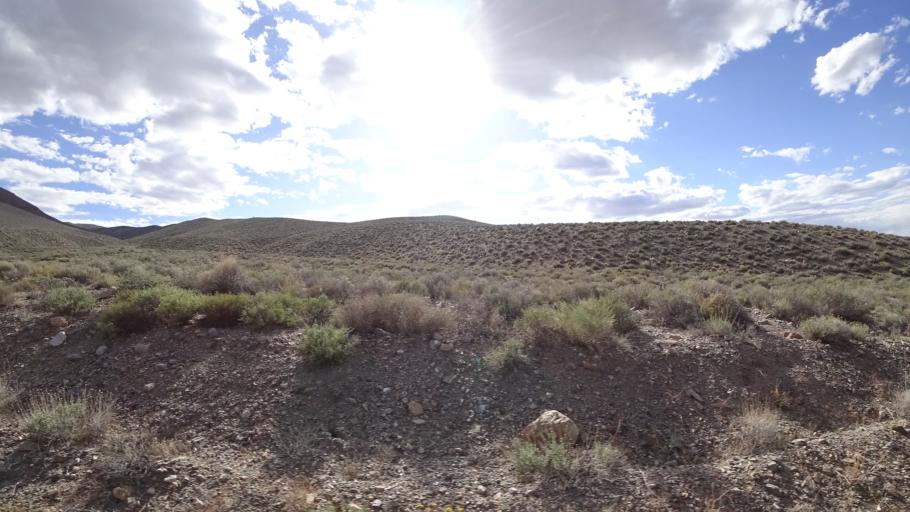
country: US
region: Nevada
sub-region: Nye County
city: Beatty
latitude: 36.4007
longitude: -117.1667
